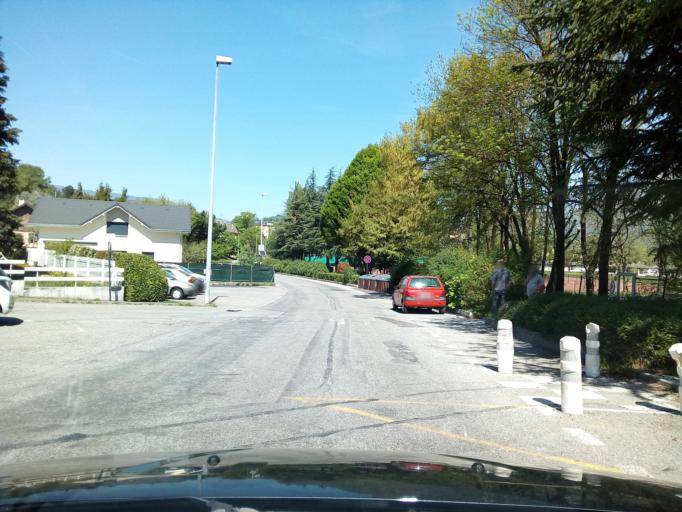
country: FR
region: Rhone-Alpes
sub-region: Departement de la Savoie
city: Barberaz
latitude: 45.5582
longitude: 5.9441
